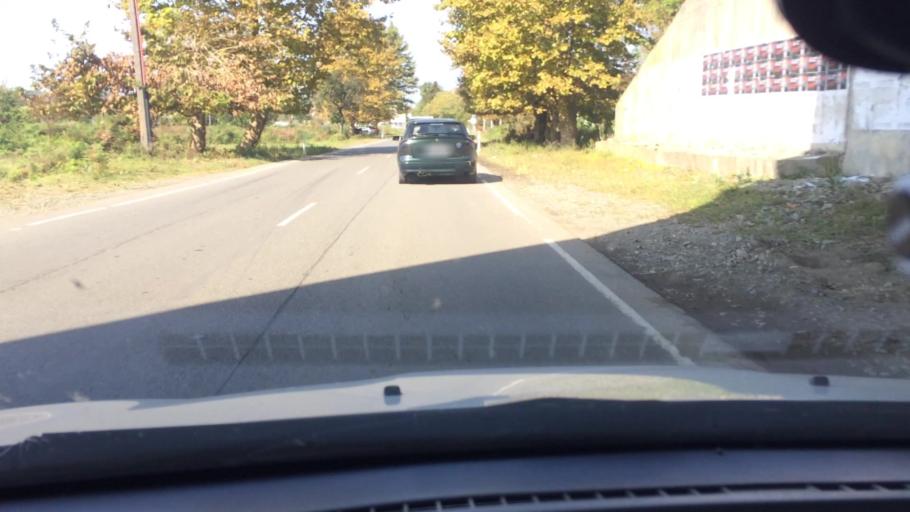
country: GE
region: Ajaria
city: Kobuleti
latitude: 41.8061
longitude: 41.7949
